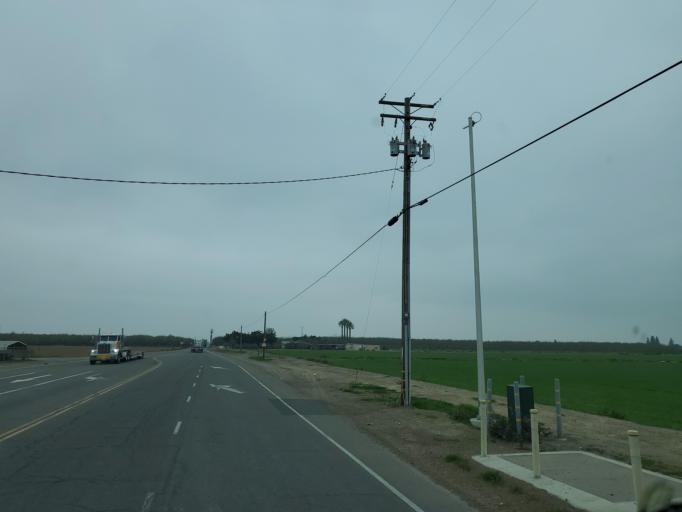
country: US
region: California
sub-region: Stanislaus County
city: Hughson
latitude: 37.5512
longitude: -120.8475
